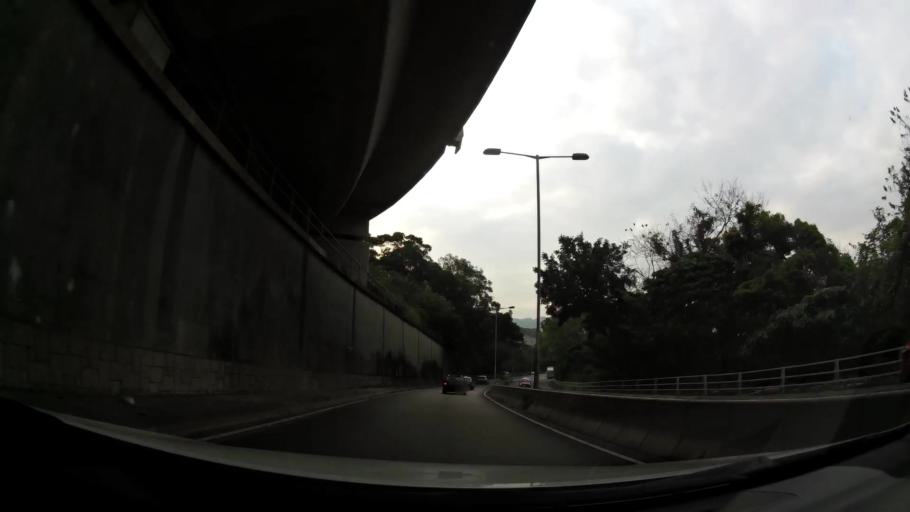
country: HK
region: Tai Po
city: Tai Po
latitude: 22.4502
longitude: 114.1553
